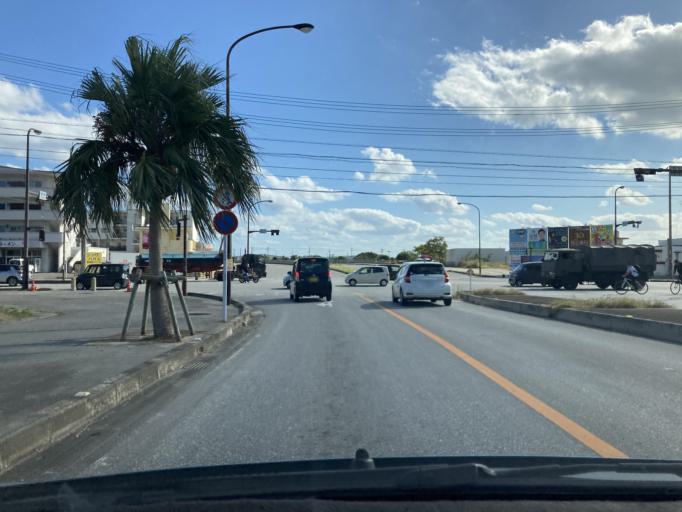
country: JP
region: Okinawa
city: Gushikawa
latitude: 26.3441
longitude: 127.8560
